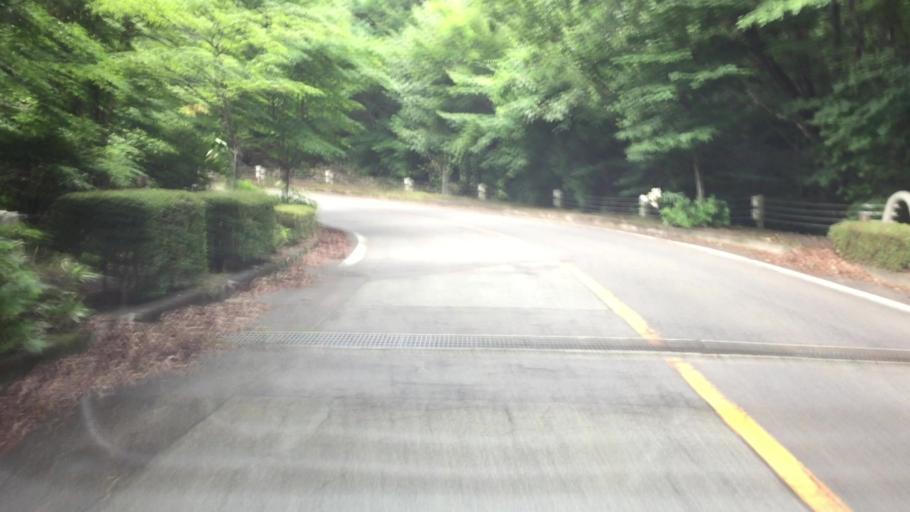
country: JP
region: Tochigi
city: Kuroiso
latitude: 37.1077
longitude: 140.0300
